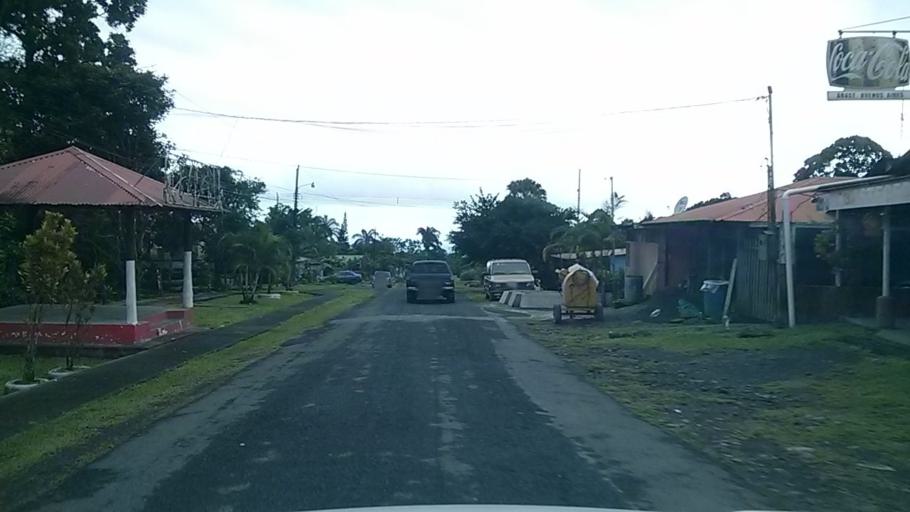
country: CR
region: Limon
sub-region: Canton de Pococi
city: Guapiles
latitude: 10.1722
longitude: -83.7837
